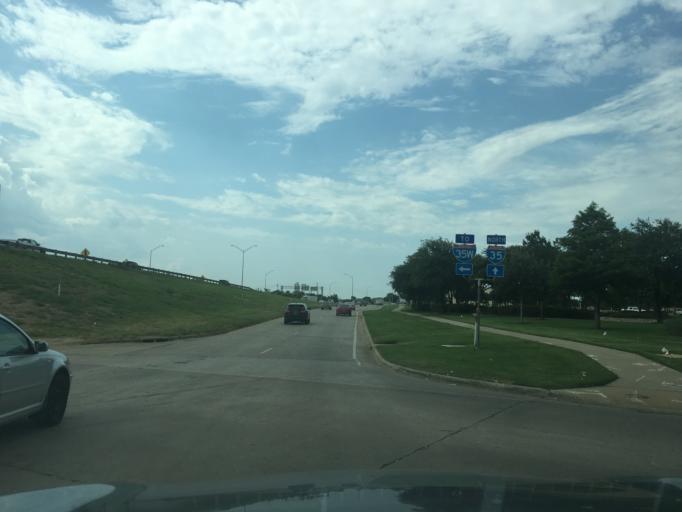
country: US
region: Texas
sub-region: Denton County
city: Denton
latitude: 33.2155
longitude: -97.1681
